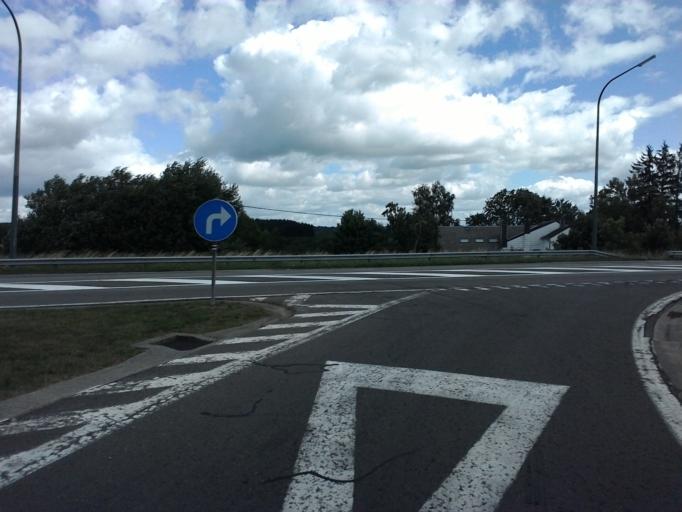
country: BE
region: Wallonia
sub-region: Province du Luxembourg
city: Leglise
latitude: 49.8079
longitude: 5.5188
